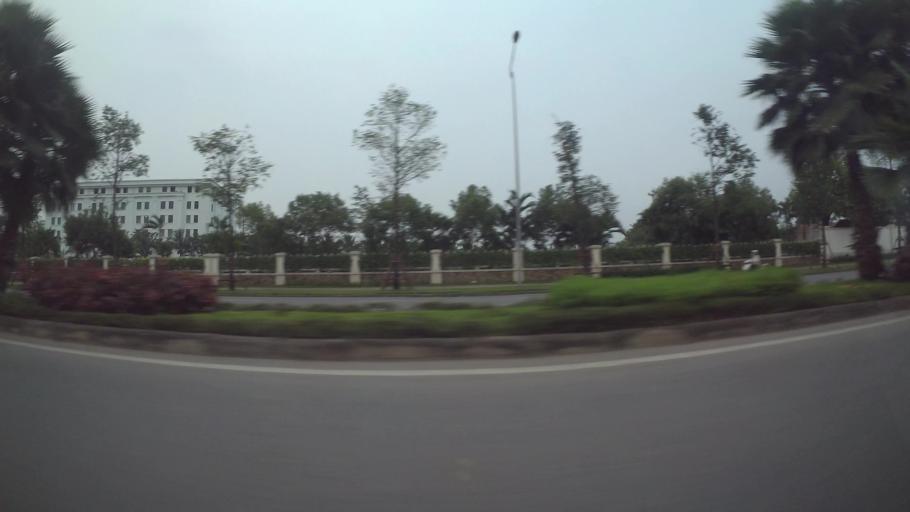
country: VN
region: Ha Noi
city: Trau Quy
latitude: 21.0492
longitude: 105.9088
